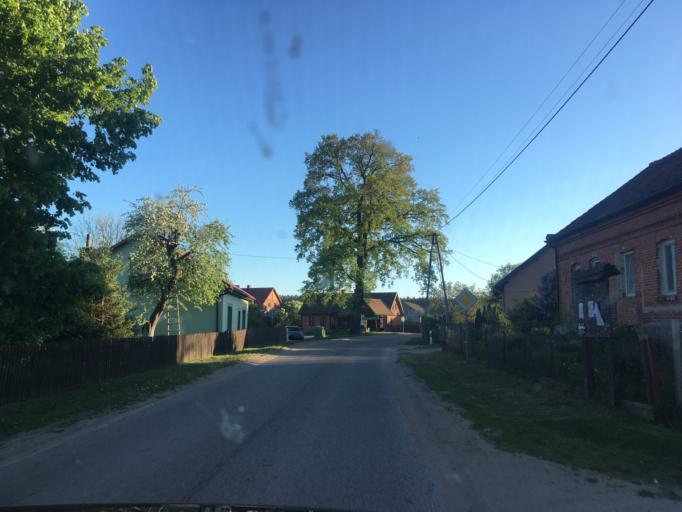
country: PL
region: Warmian-Masurian Voivodeship
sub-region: Powiat mragowski
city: Piecki
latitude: 53.6999
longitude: 21.3002
